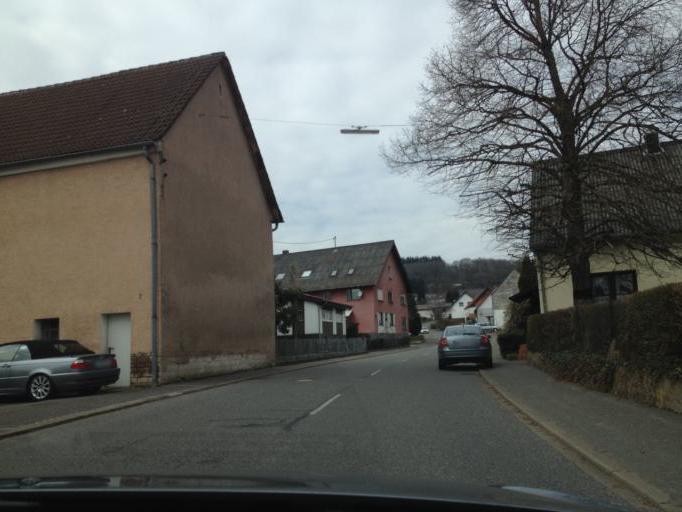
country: DE
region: Saarland
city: Freisen
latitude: 49.5547
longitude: 7.2477
